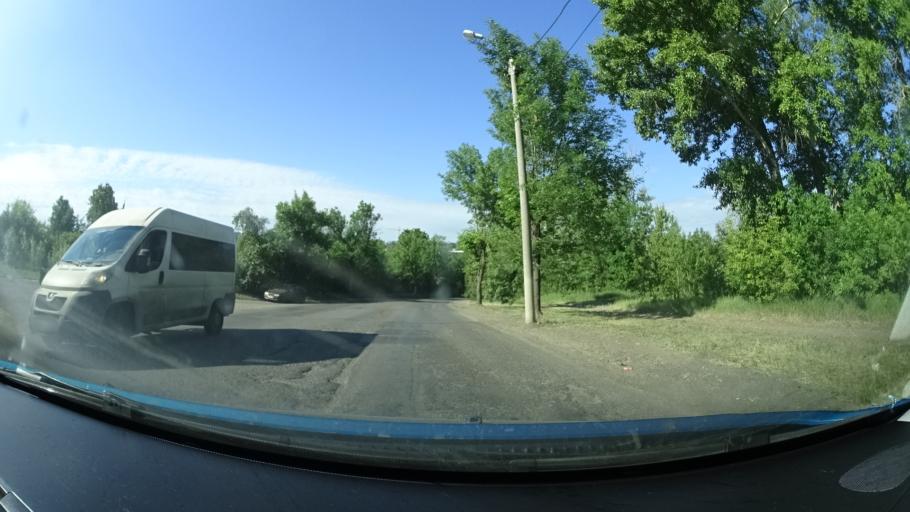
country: RU
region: Bashkortostan
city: Ufa
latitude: 54.8344
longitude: 56.0756
